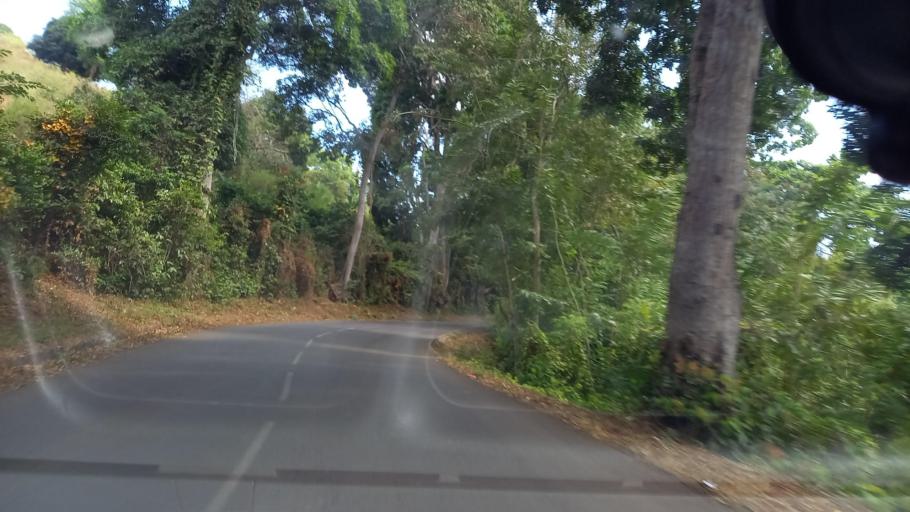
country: YT
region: Mamoudzou
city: Mamoudzou
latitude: -12.7970
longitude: 45.2009
